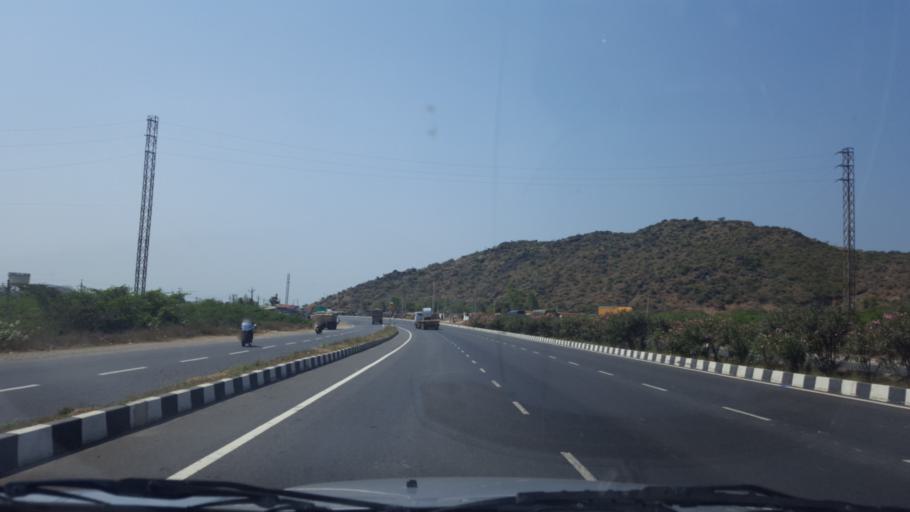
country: IN
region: Andhra Pradesh
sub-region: Prakasam
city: Addanki
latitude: 15.7344
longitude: 80.0121
